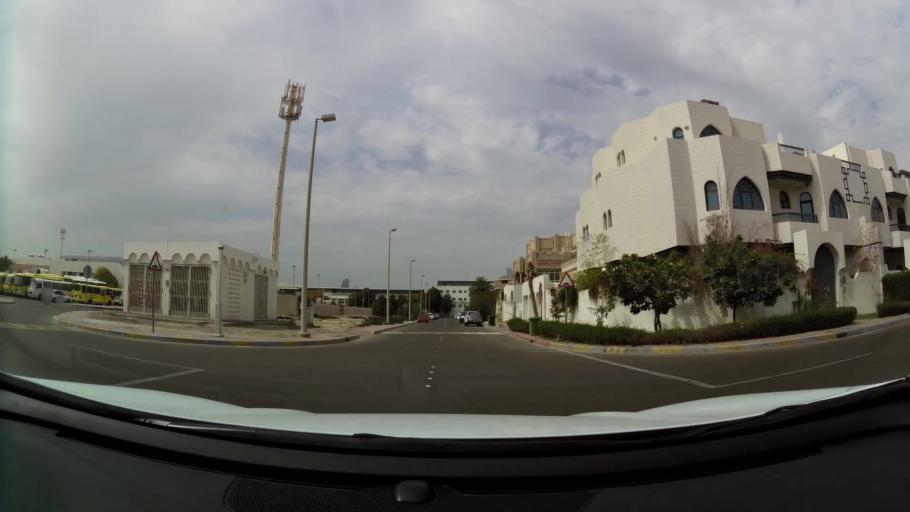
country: AE
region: Abu Dhabi
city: Abu Dhabi
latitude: 24.4613
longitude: 54.3674
